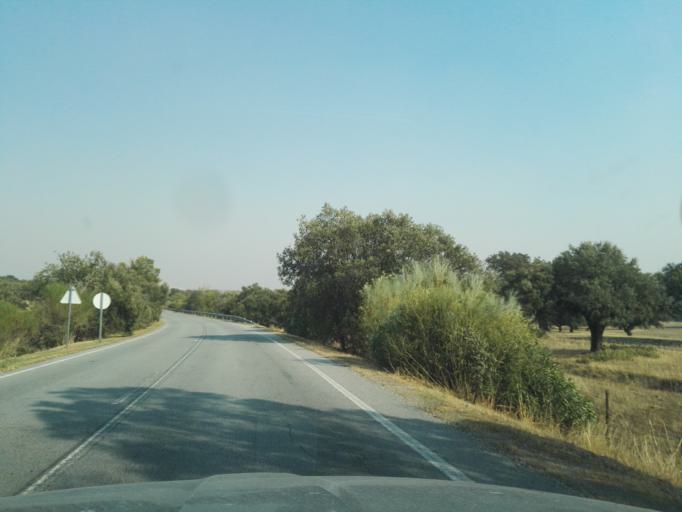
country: PT
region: Portalegre
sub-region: Campo Maior
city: Campo Maior
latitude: 38.9934
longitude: -7.1580
